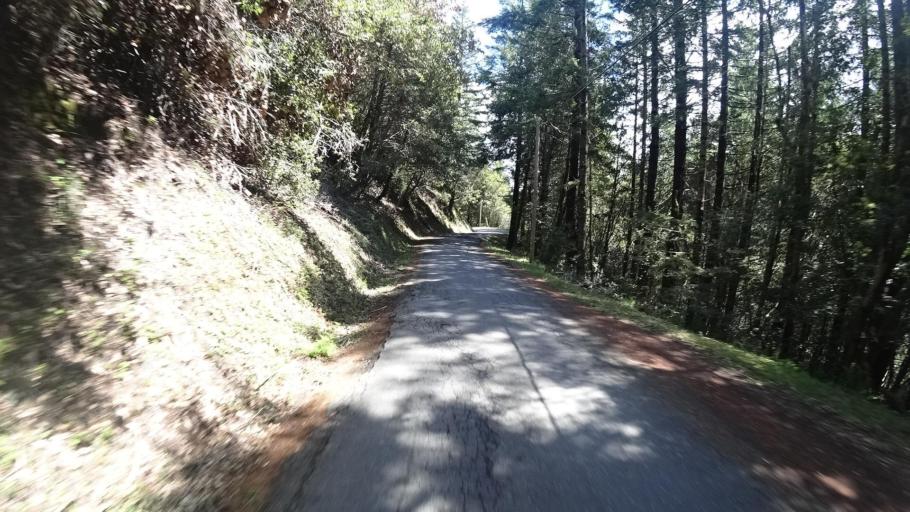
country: US
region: California
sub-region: Humboldt County
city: Blue Lake
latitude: 40.7615
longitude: -123.9523
